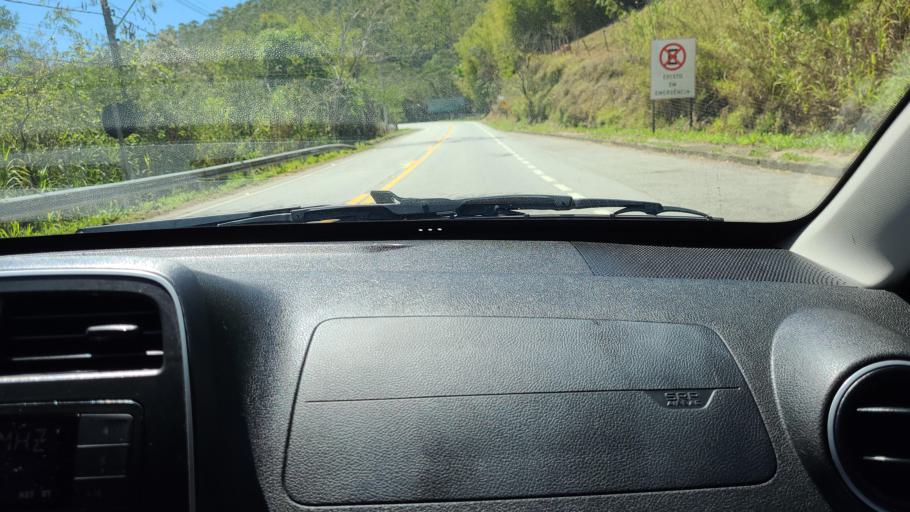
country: BR
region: Sao Paulo
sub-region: Tremembe
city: Tremembe
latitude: -22.8757
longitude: -45.5805
